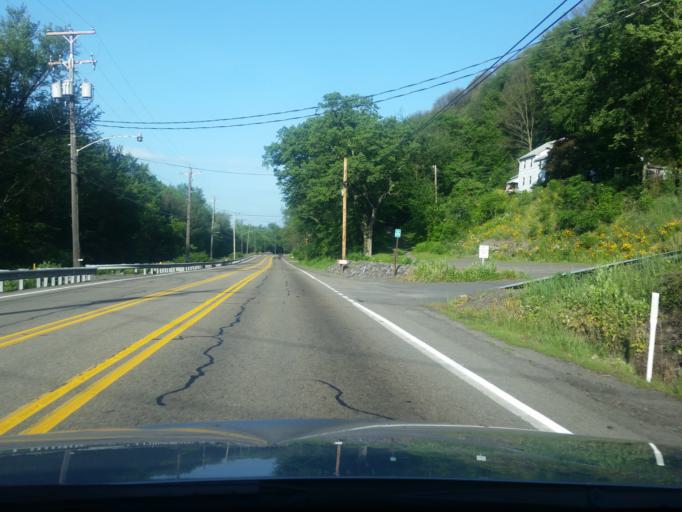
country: US
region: Pennsylvania
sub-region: Luzerne County
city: Nanticoke
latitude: 41.2209
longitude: -75.9873
